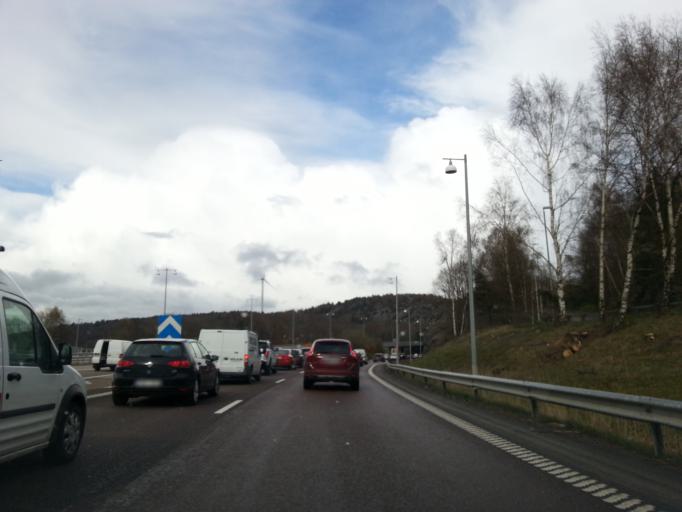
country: SE
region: Vaestra Goetaland
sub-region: Goteborg
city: Hammarkullen
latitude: 57.7863
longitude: 12.0112
